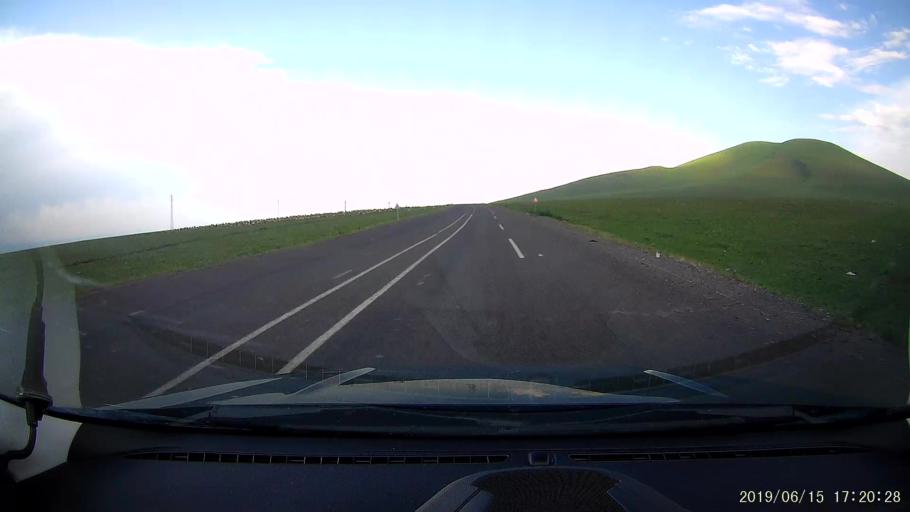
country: TR
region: Kars
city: Kars
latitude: 40.6162
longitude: 43.3026
